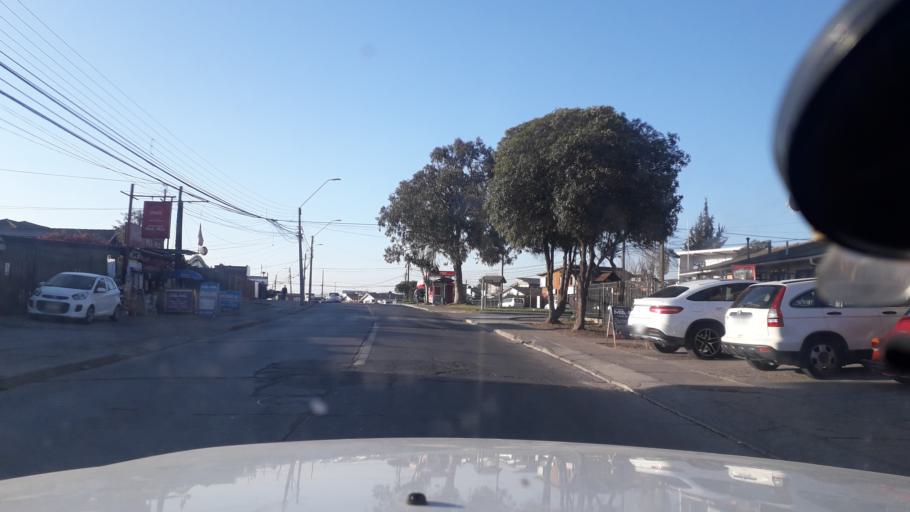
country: CL
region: Valparaiso
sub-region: Provincia de Valparaiso
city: Vina del Mar
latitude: -32.9279
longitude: -71.5172
